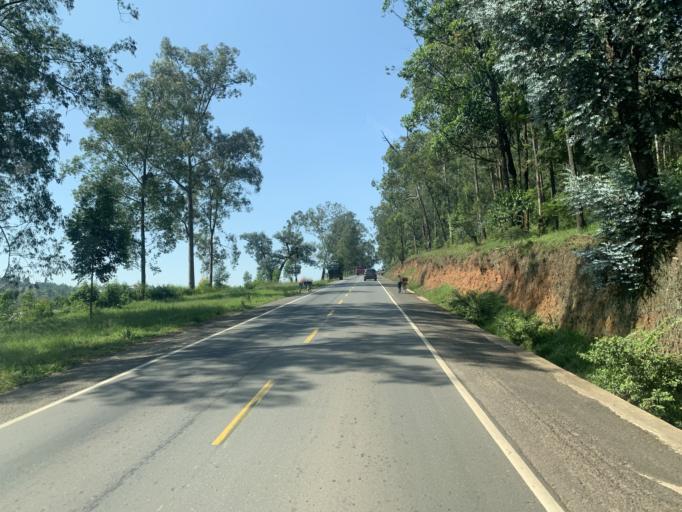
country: RW
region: Kigali
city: Kigali
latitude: -1.9916
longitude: 29.9284
